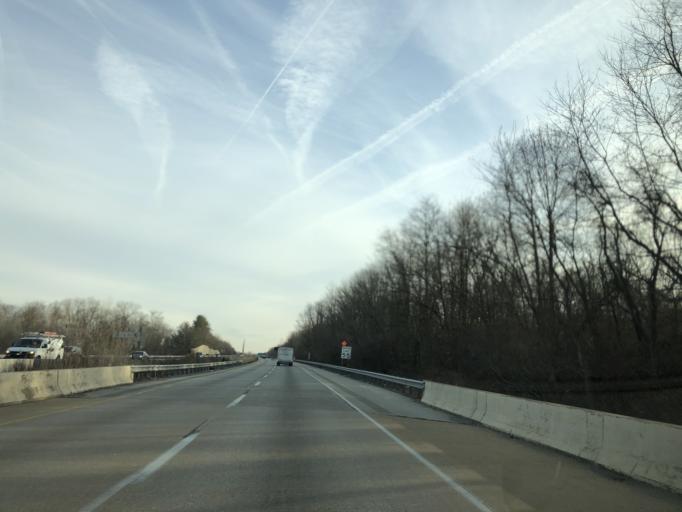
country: US
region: Pennsylvania
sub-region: Chester County
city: Exton
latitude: 40.0239
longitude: -75.6091
